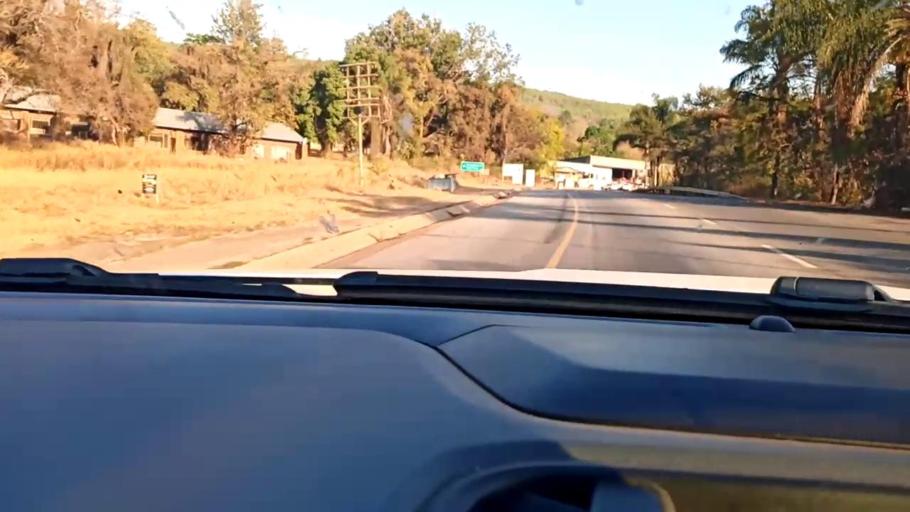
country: ZA
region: Limpopo
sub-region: Mopani District Municipality
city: Duiwelskloof
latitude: -23.6914
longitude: 30.1463
